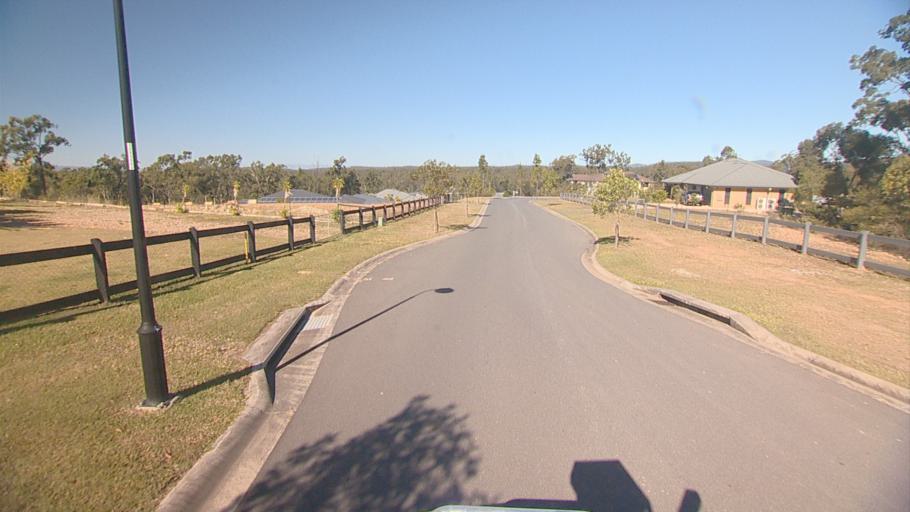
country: AU
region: Queensland
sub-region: Ipswich
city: Springfield Lakes
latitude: -27.7222
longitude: 152.9137
